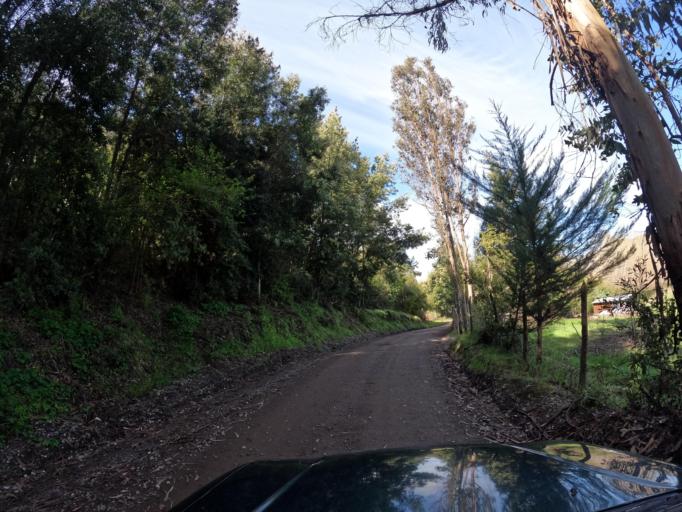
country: CL
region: Biobio
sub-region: Provincia de Concepcion
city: Chiguayante
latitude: -37.0685
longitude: -72.9021
